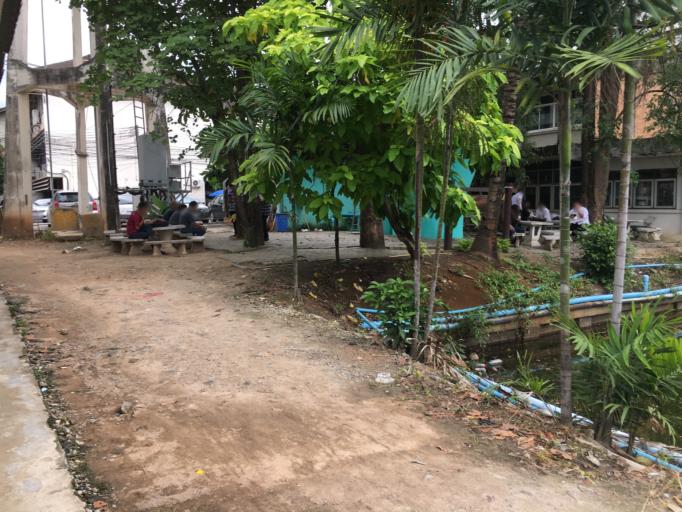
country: TH
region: Chiang Mai
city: Chiang Mai
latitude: 18.8069
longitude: 98.9878
